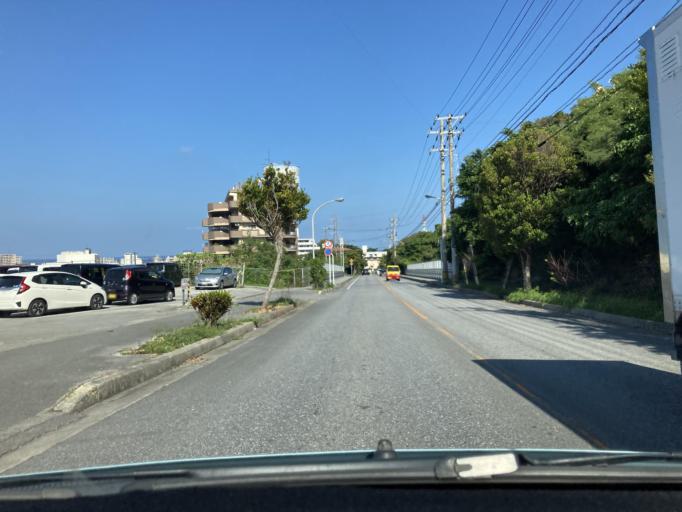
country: JP
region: Okinawa
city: Ginowan
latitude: 26.2538
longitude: 127.7246
